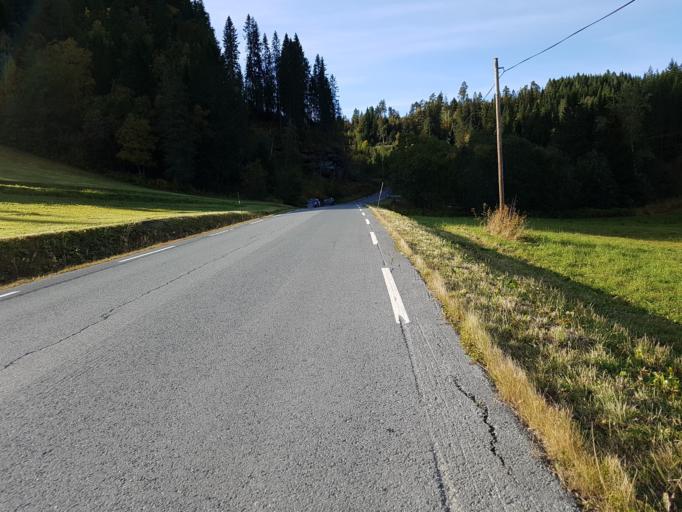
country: NO
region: Sor-Trondelag
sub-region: Klaebu
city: Klaebu
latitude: 63.3454
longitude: 10.5407
